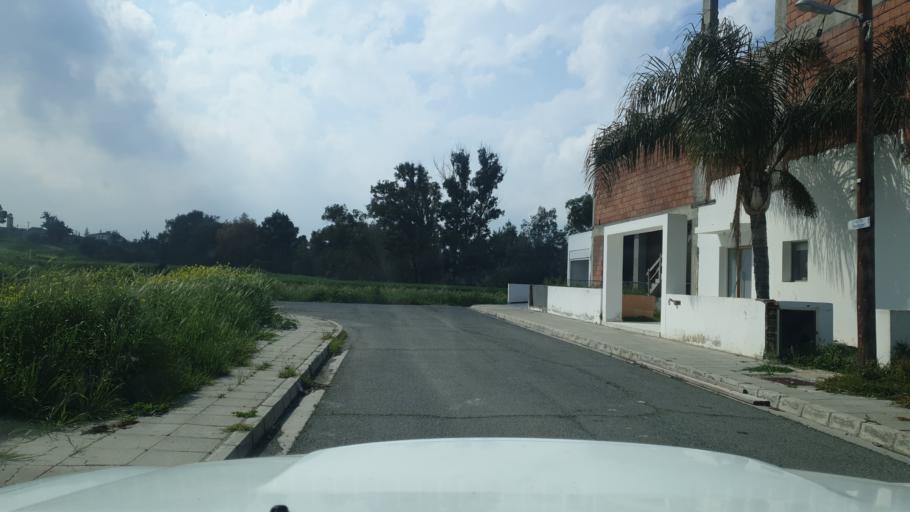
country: CY
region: Lefkosia
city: Kato Deftera
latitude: 35.0901
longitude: 33.2810
